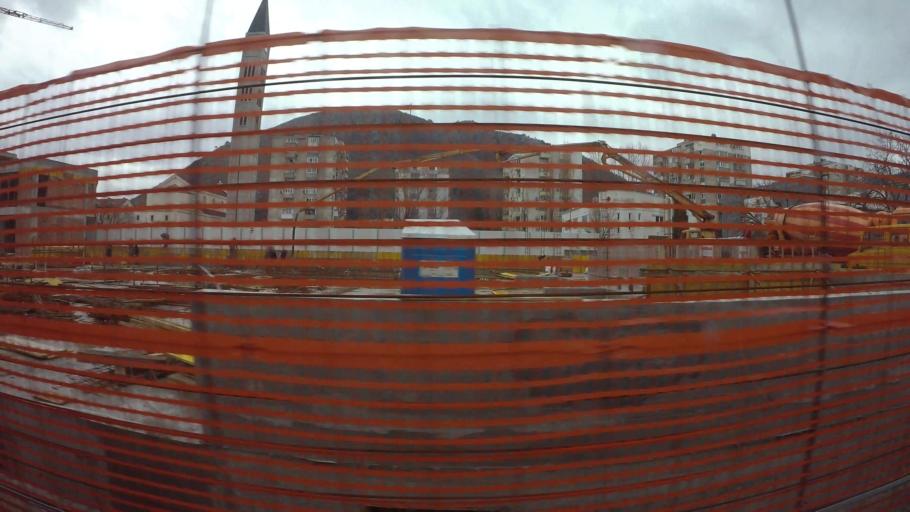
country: BA
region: Federation of Bosnia and Herzegovina
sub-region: Hercegovacko-Bosanski Kanton
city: Mostar
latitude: 43.3393
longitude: 17.8082
